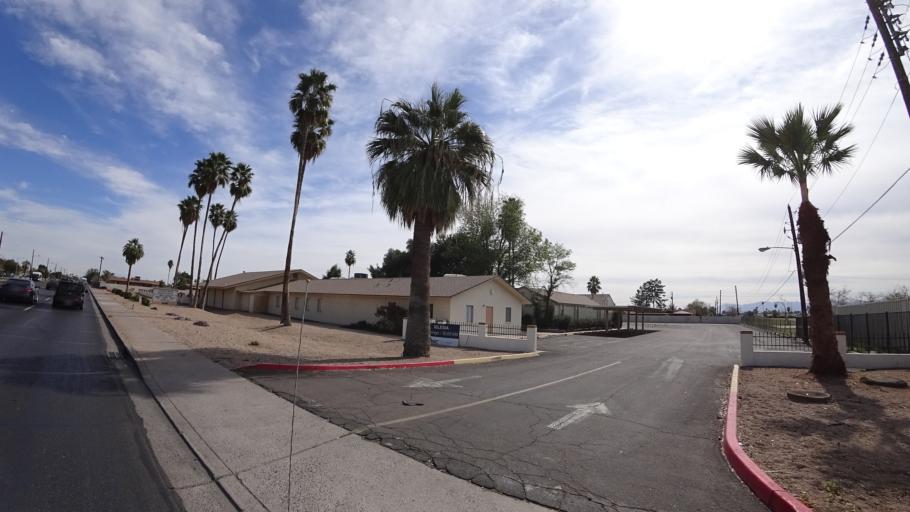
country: US
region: Arizona
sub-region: Maricopa County
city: Glendale
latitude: 33.4805
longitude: -112.1840
